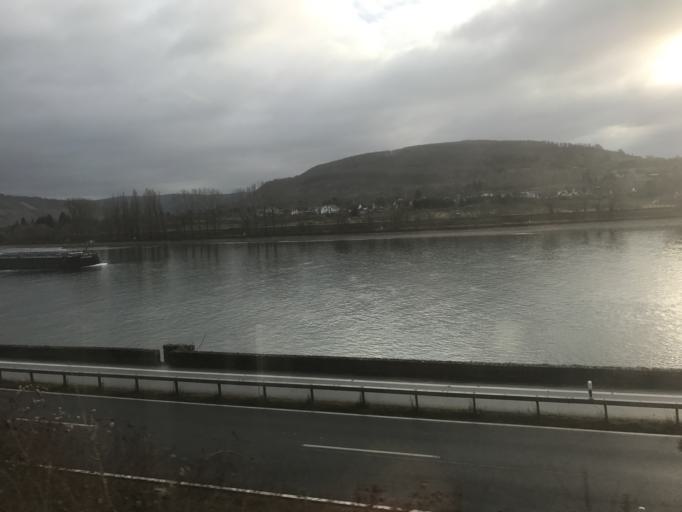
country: DE
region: Rheinland-Pfalz
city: Filsen
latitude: 50.2441
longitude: 7.5772
